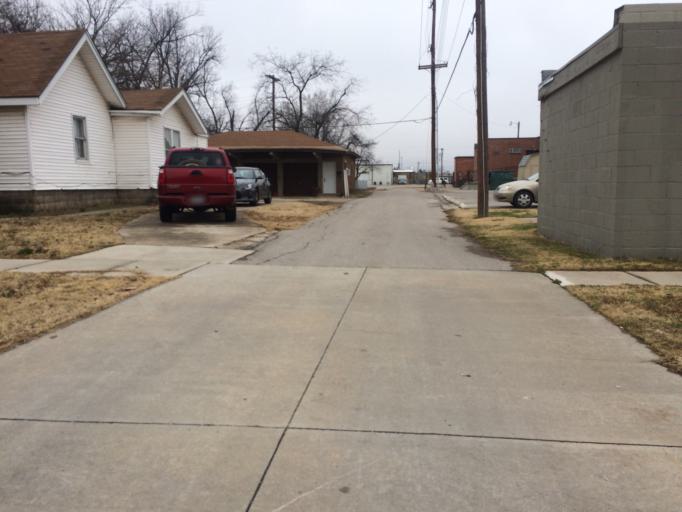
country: US
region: Oklahoma
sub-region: Cleveland County
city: Norman
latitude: 35.2176
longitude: -97.4427
